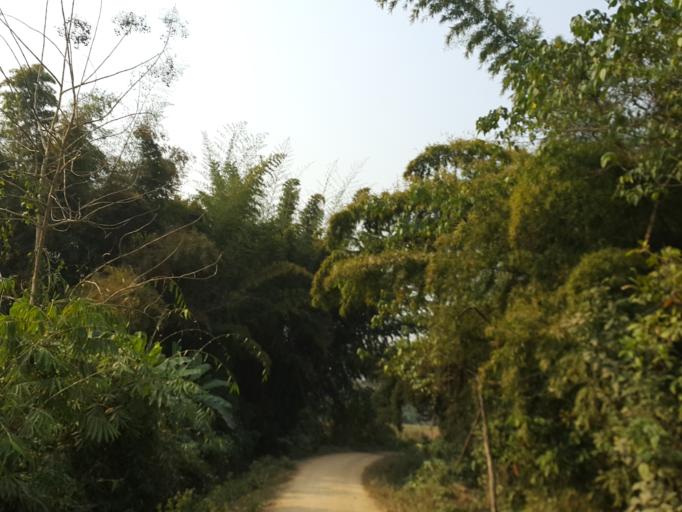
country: TH
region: Lamphun
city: Li
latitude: 17.6076
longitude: 98.9635
